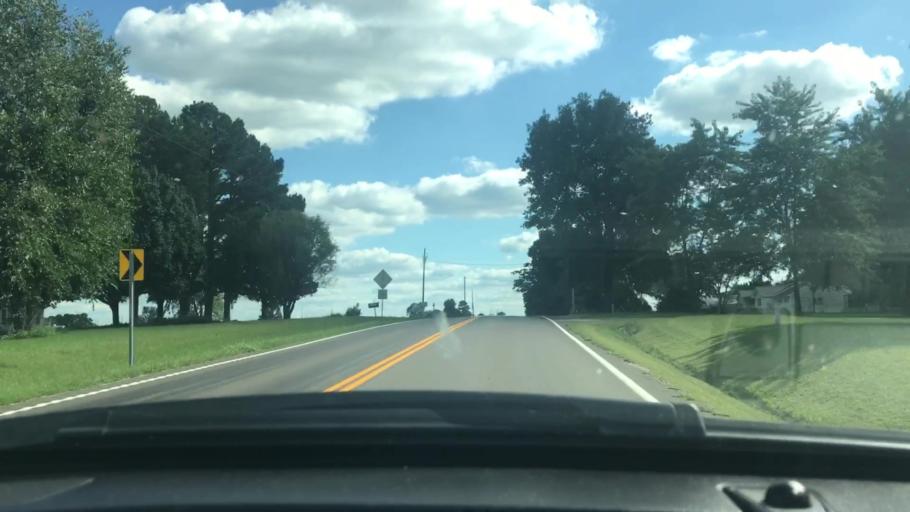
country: US
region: Missouri
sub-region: Wright County
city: Mountain Grove
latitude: 37.2517
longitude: -92.3003
